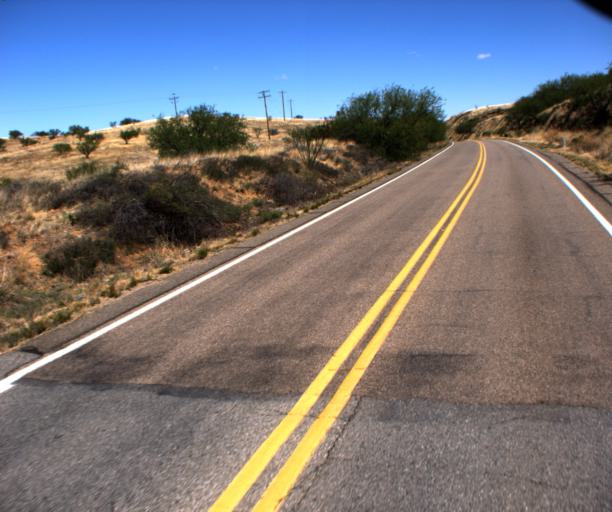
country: US
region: Arizona
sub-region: Santa Cruz County
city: Rio Rico
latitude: 31.4663
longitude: -110.8222
